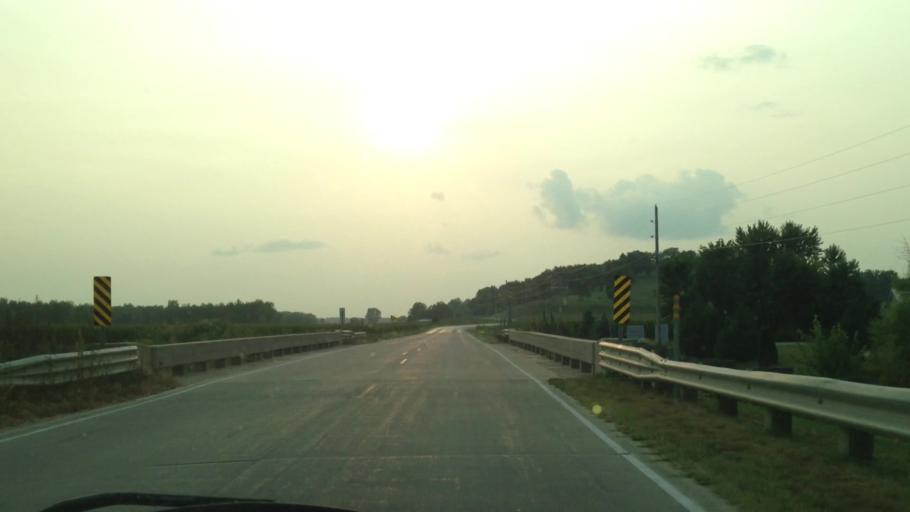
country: US
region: Iowa
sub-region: Iowa County
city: Marengo
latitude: 41.8281
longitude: -92.0780
